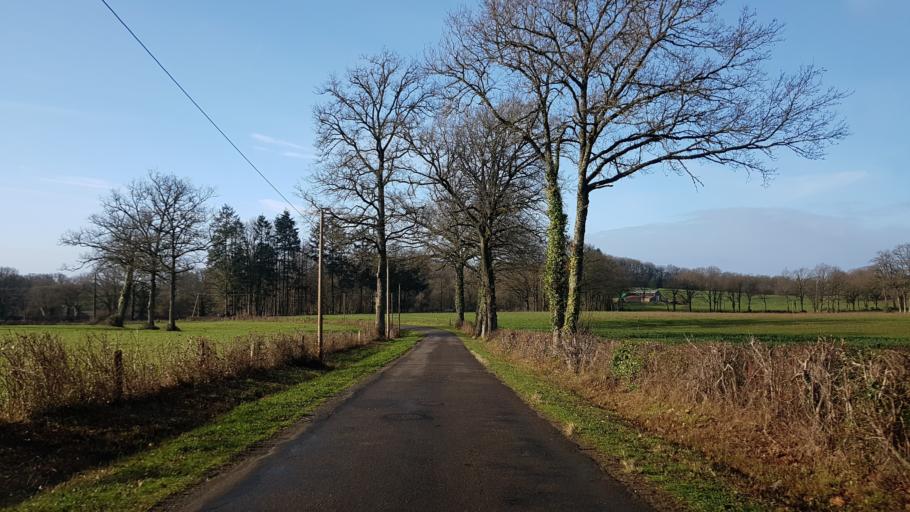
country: FR
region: Poitou-Charentes
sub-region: Departement de la Charente
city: Etagnac
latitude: 45.9082
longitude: 0.8122
